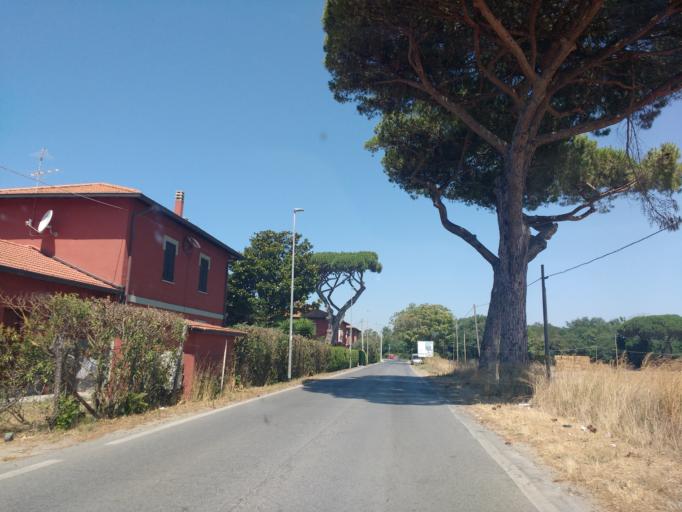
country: IT
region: Latium
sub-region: Citta metropolitana di Roma Capitale
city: Maccarese
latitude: 41.8618
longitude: 12.2114
